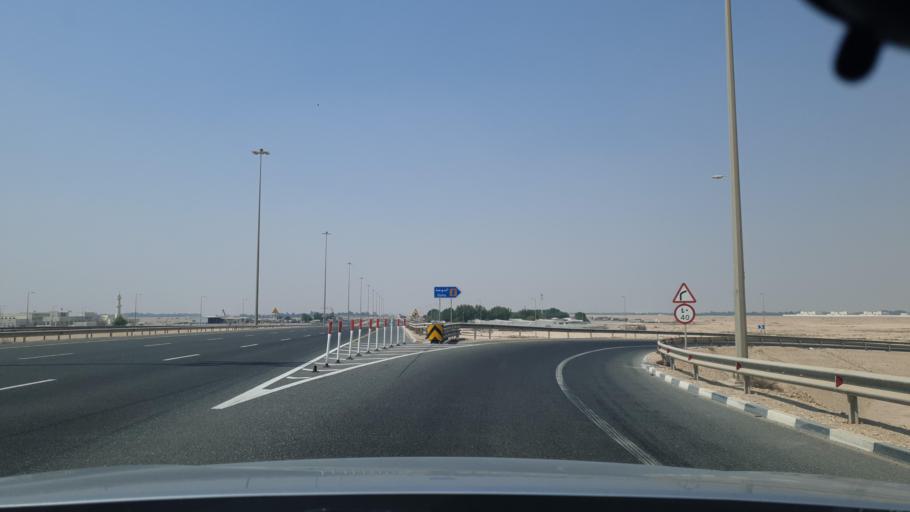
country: QA
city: Al Ghuwayriyah
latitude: 25.8296
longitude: 51.3485
